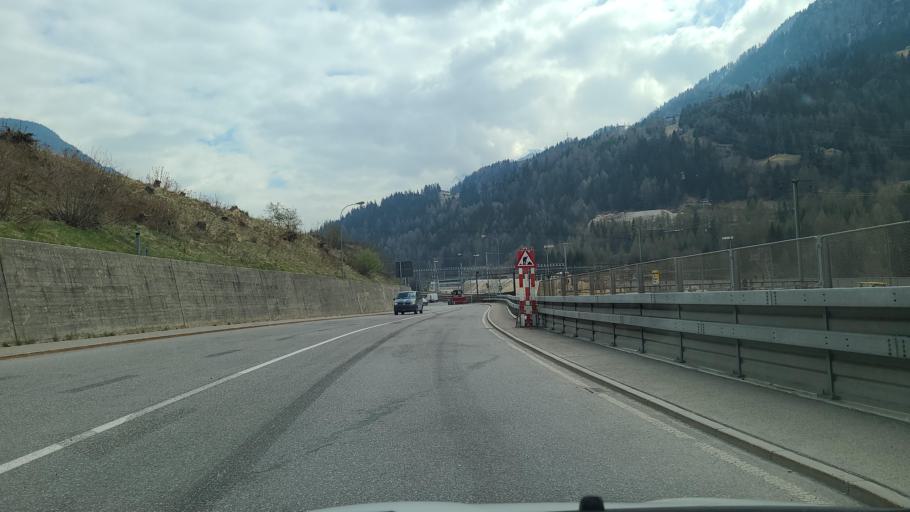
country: CH
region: Ticino
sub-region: Leventina District
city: Airolo
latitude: 46.5284
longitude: 8.6036
